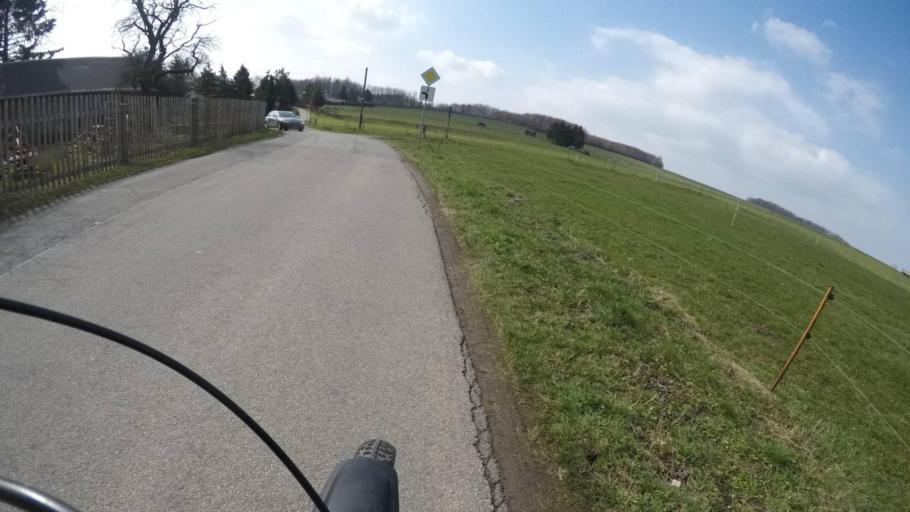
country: DE
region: Saxony
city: Limbach-Oberfrohna
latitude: 50.8743
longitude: 12.7354
